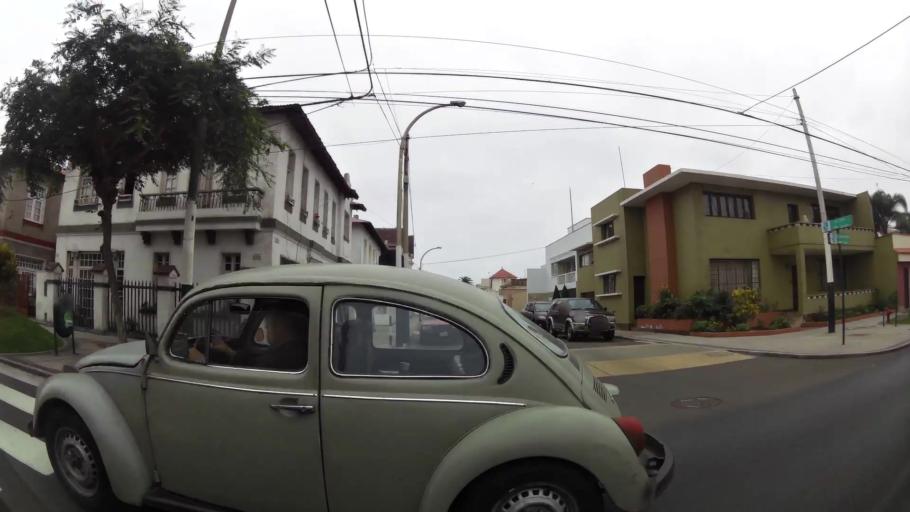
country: PE
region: Callao
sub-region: Callao
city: Callao
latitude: -12.0715
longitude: -77.1636
